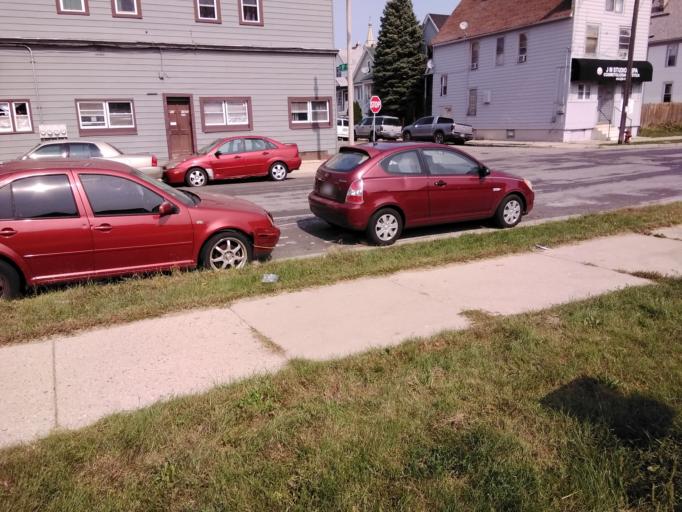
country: US
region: Wisconsin
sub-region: Milwaukee County
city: West Milwaukee
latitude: 43.0046
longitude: -87.9326
